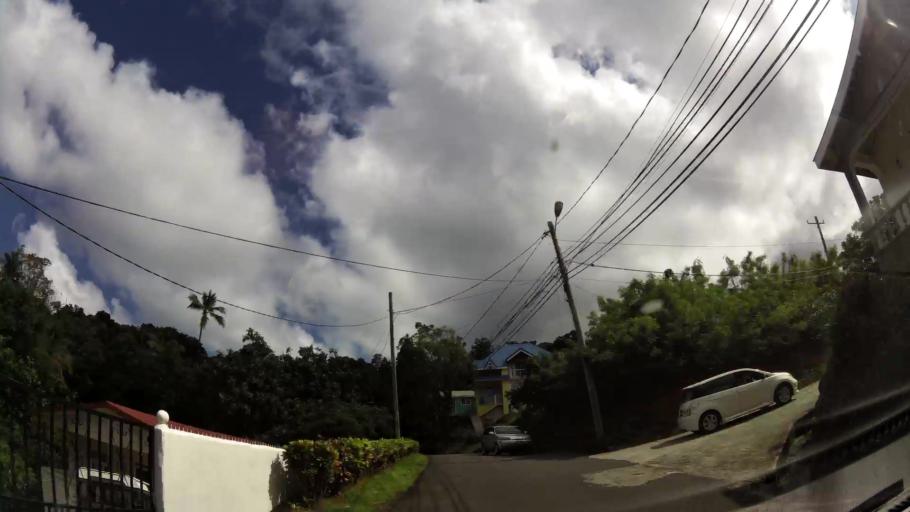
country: DM
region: Saint John
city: Portsmouth
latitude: 15.6162
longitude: -61.4634
